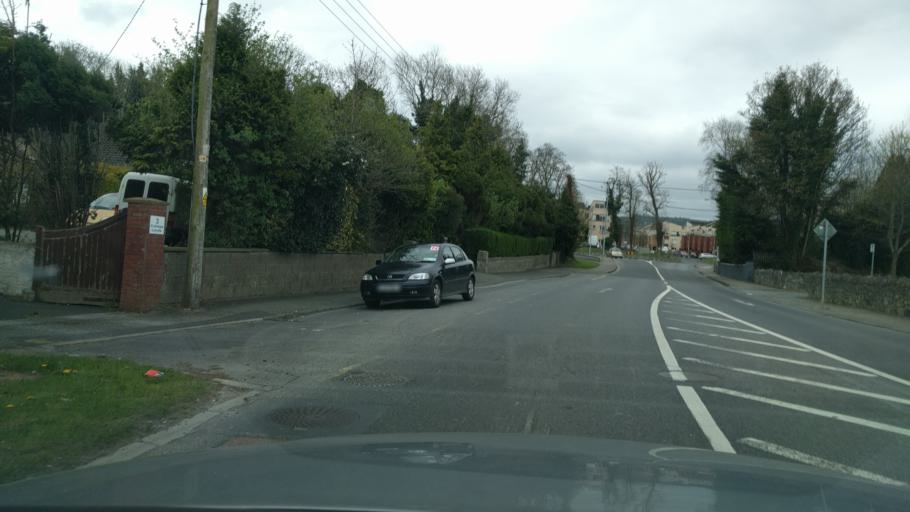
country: IE
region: Leinster
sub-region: South Dublin
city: Saggart
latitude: 53.2828
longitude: -6.4524
